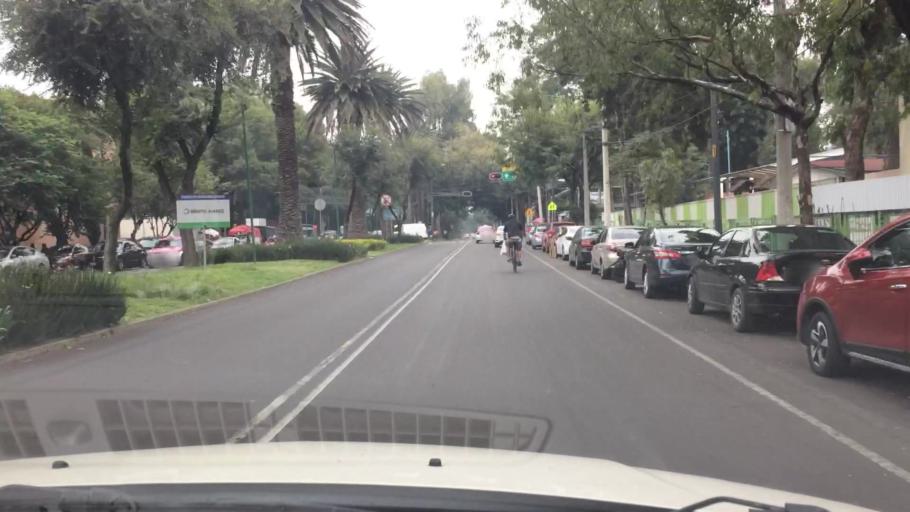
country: MX
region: Mexico City
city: Colonia del Valle
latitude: 19.3692
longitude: -99.1553
